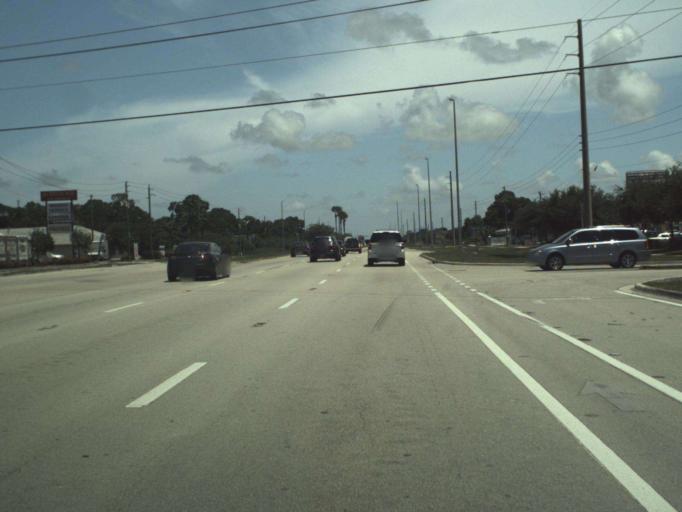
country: US
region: Florida
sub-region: Saint Lucie County
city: River Park
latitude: 27.3163
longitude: -80.3149
